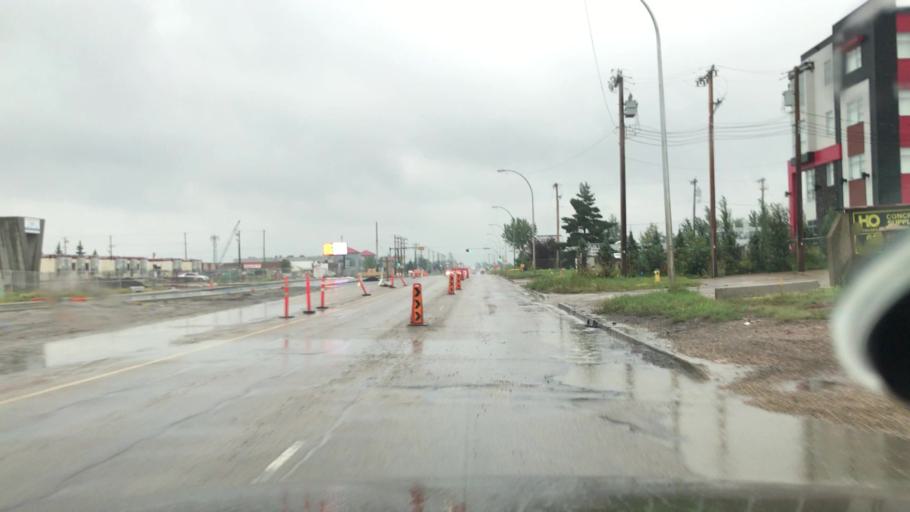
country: CA
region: Alberta
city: Edmonton
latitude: 53.4996
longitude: -113.4426
